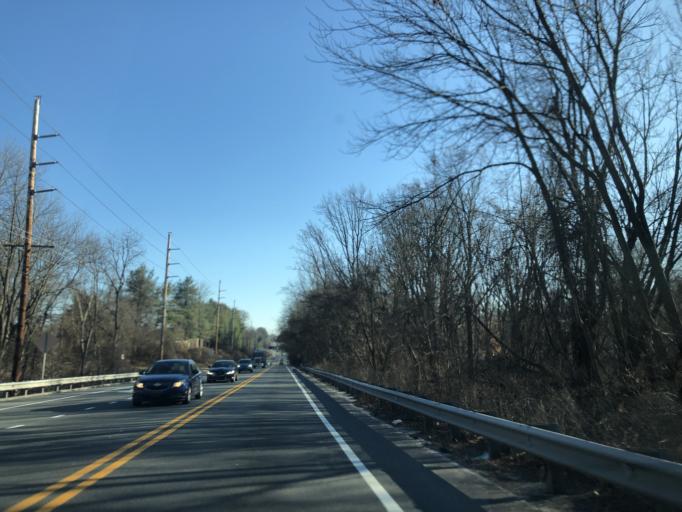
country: US
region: Delaware
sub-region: New Castle County
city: Hockessin
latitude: 39.7839
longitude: -75.6834
